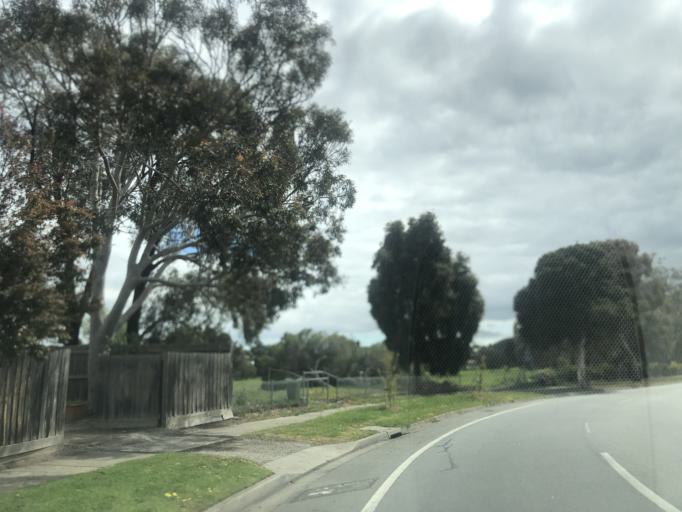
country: AU
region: Victoria
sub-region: Casey
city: Endeavour Hills
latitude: -37.9793
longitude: 145.2452
